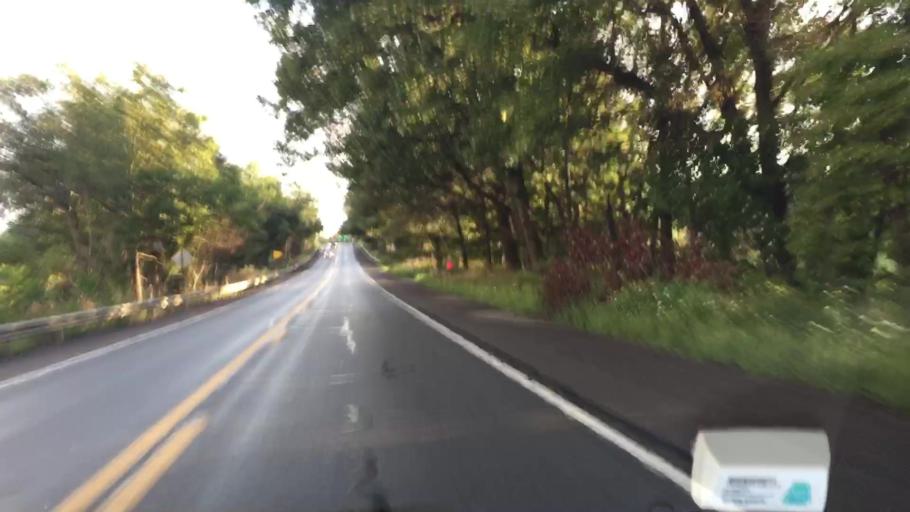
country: US
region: Pennsylvania
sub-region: Butler County
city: Meridian
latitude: 40.8128
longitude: -80.0120
